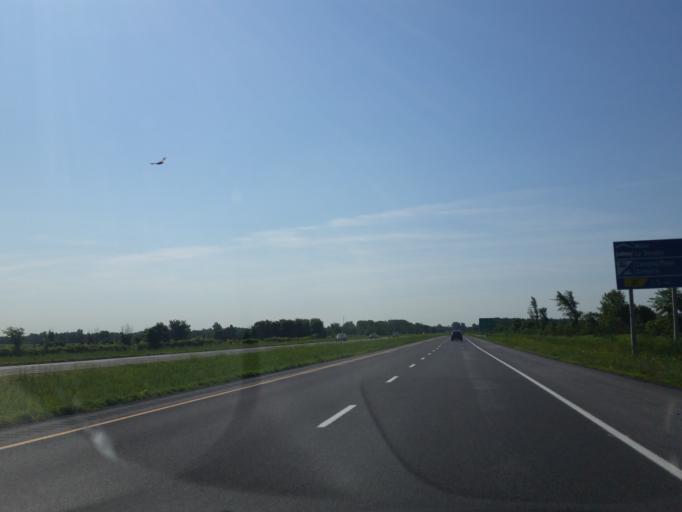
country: CA
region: Quebec
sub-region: Monteregie
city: Napierville
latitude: 45.2089
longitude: -73.4717
